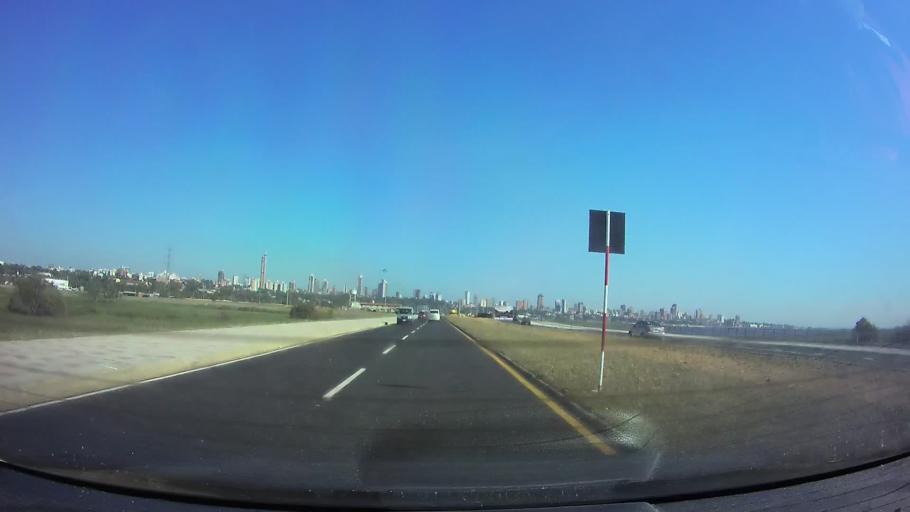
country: PY
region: Asuncion
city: Asuncion
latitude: -25.2678
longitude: -57.6112
